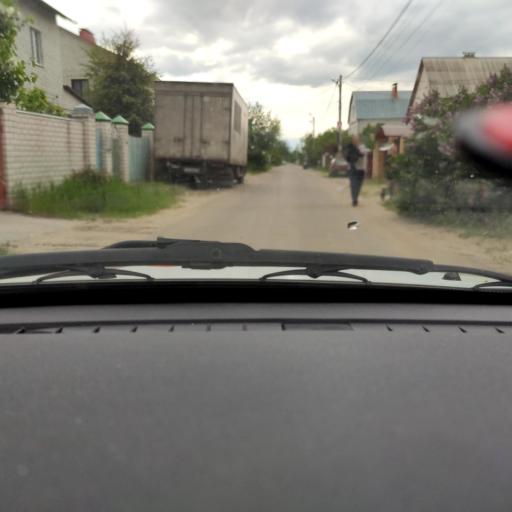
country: RU
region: Voronezj
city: Podgornoye
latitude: 51.7457
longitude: 39.1604
